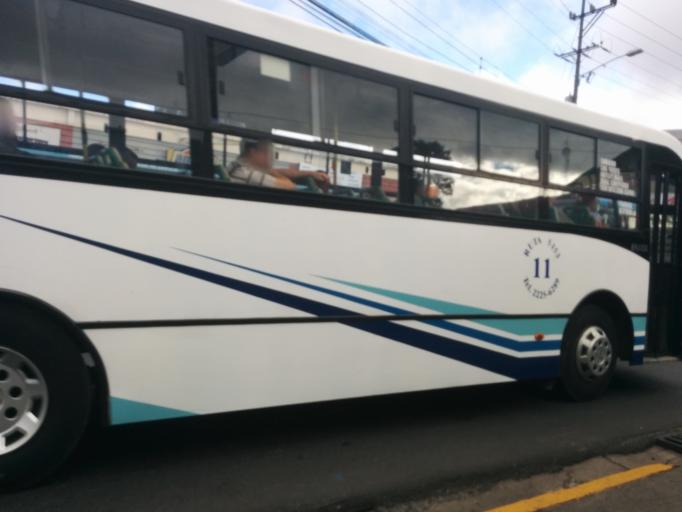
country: CR
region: San Jose
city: San Pedro
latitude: 9.9319
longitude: -84.0506
